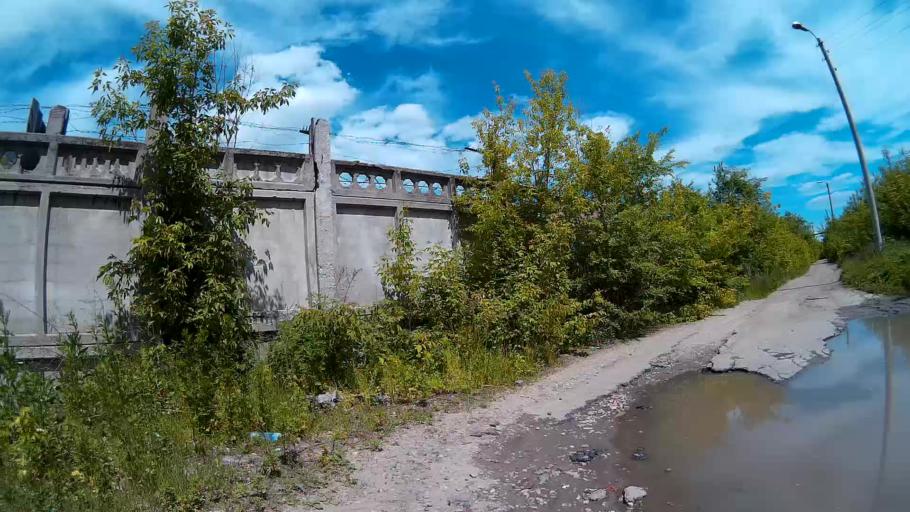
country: RU
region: Ulyanovsk
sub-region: Ulyanovskiy Rayon
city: Ulyanovsk
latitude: 54.2800
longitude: 48.3568
